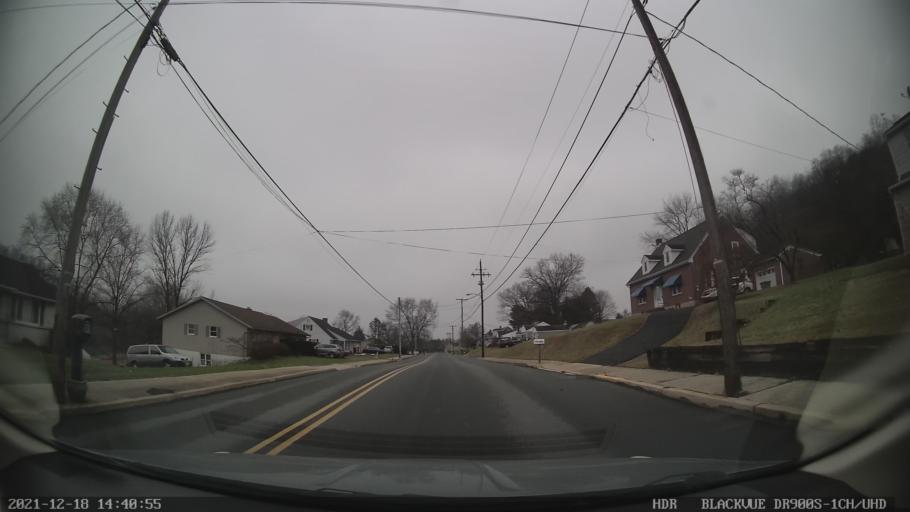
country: US
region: Pennsylvania
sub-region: Berks County
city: New Berlinville
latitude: 40.3659
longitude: -75.6293
